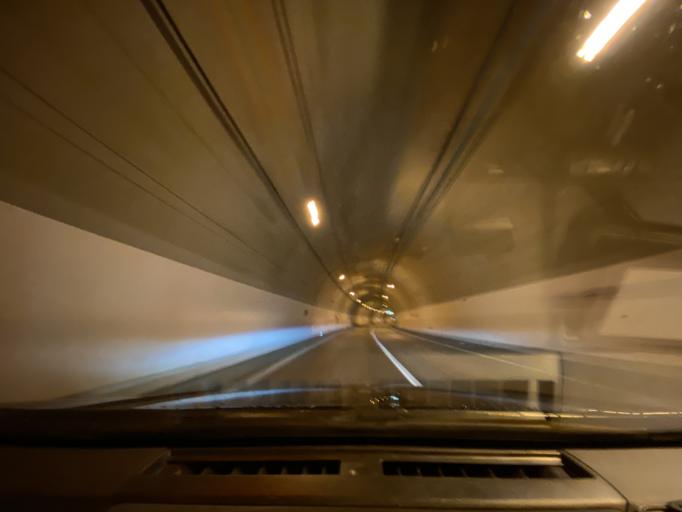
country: JP
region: Hokkaido
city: Ishikari
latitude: 43.4681
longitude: 141.3986
